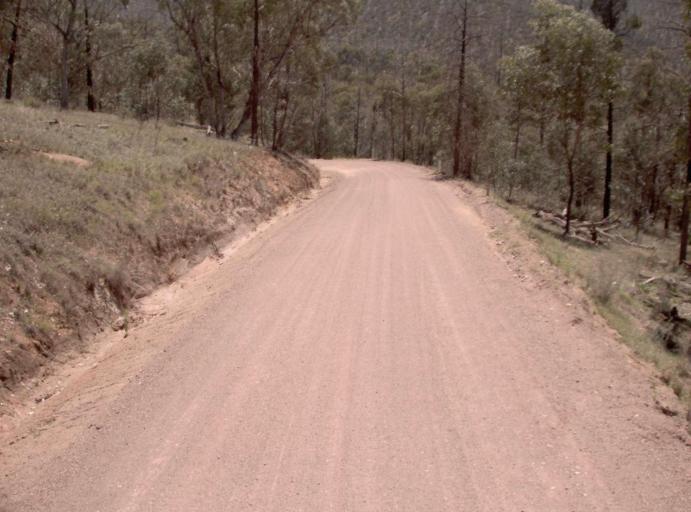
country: AU
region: New South Wales
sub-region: Snowy River
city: Jindabyne
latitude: -36.9261
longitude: 148.3900
